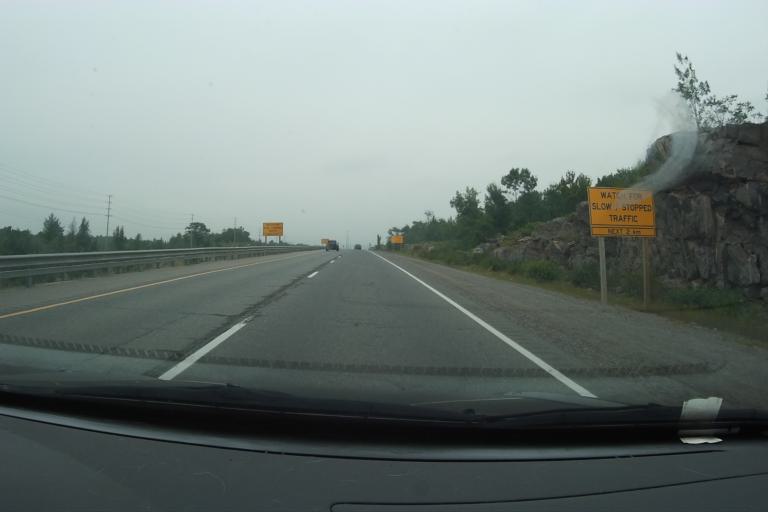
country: CA
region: Ontario
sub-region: Nipissing District
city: North Bay
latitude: 46.2947
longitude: -79.4232
